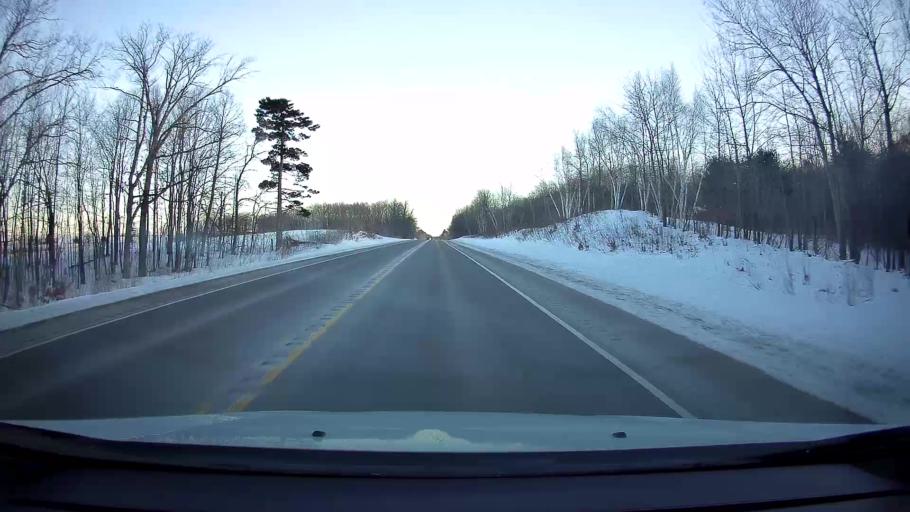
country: US
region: Wisconsin
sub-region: Washburn County
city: Shell Lake
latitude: 45.6858
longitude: -91.9775
